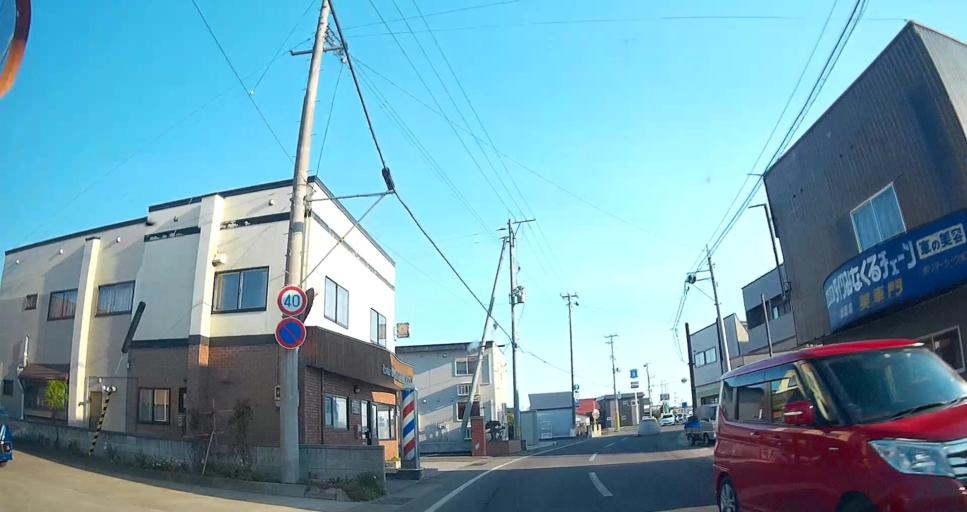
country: JP
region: Aomori
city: Mutsu
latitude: 41.2870
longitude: 141.2116
